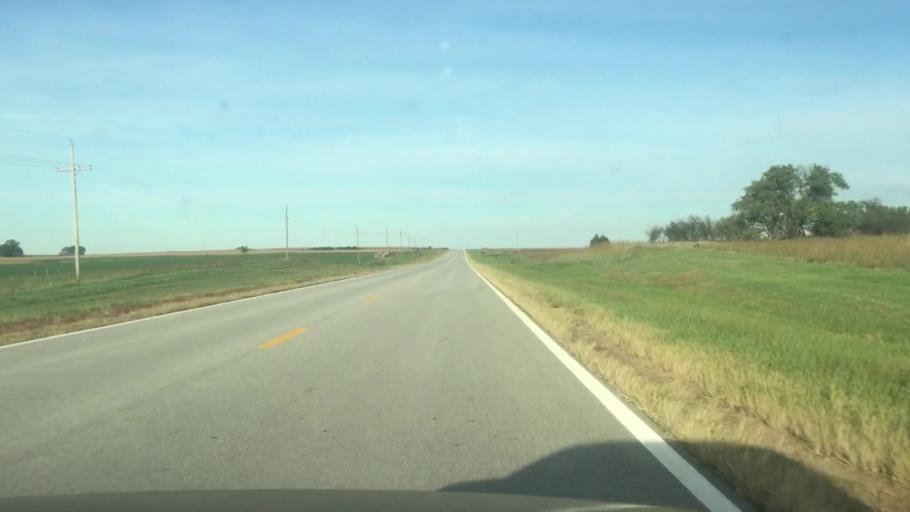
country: US
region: Nebraska
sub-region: Gage County
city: Wymore
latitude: 40.0450
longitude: -96.7193
